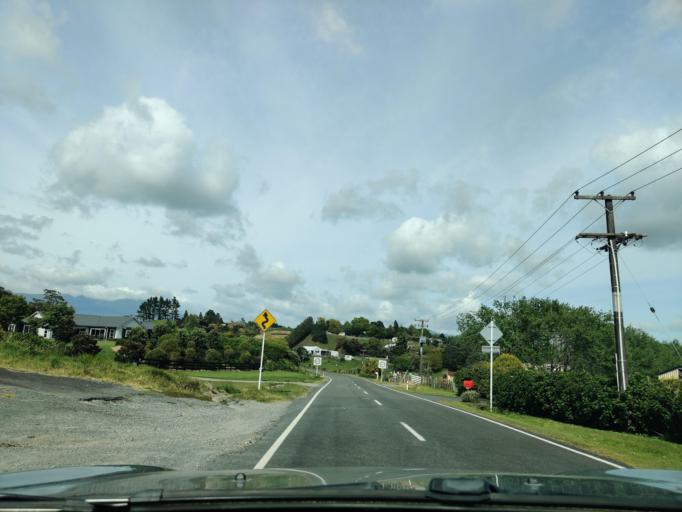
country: NZ
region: Taranaki
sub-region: New Plymouth District
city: New Plymouth
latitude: -39.0940
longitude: 174.1044
